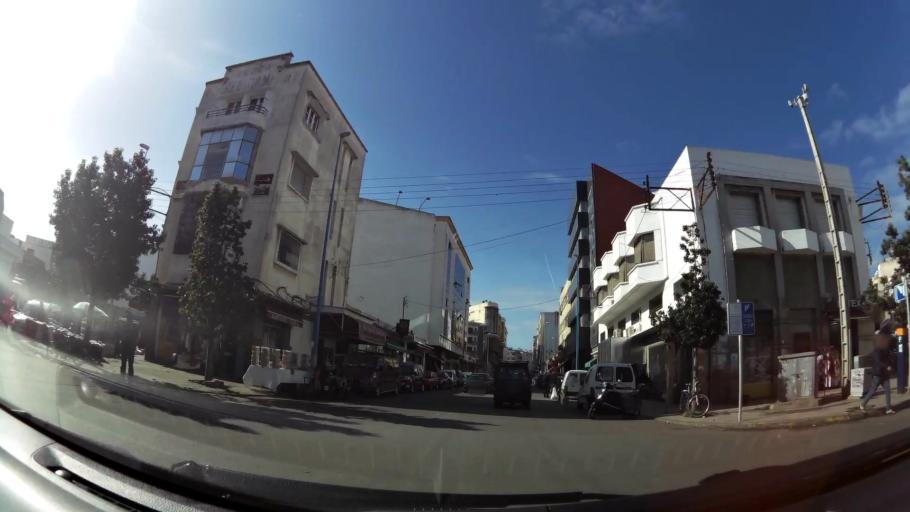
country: MA
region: Grand Casablanca
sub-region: Casablanca
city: Casablanca
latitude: 33.5920
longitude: -7.6112
